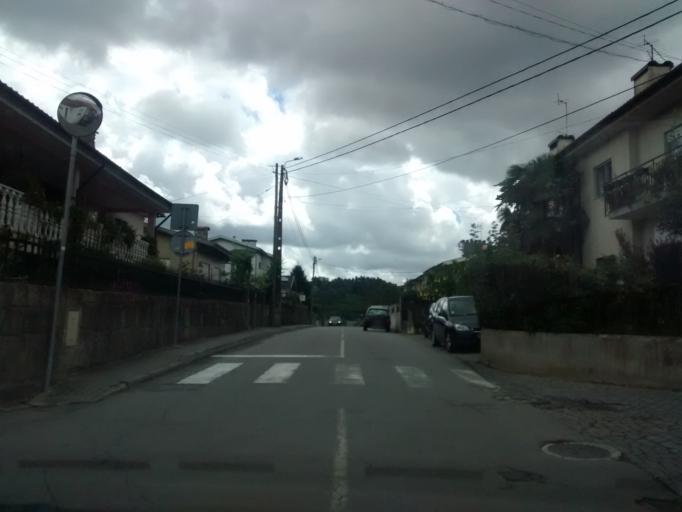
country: PT
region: Braga
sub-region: Braga
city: Braga
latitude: 41.5694
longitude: -8.4346
